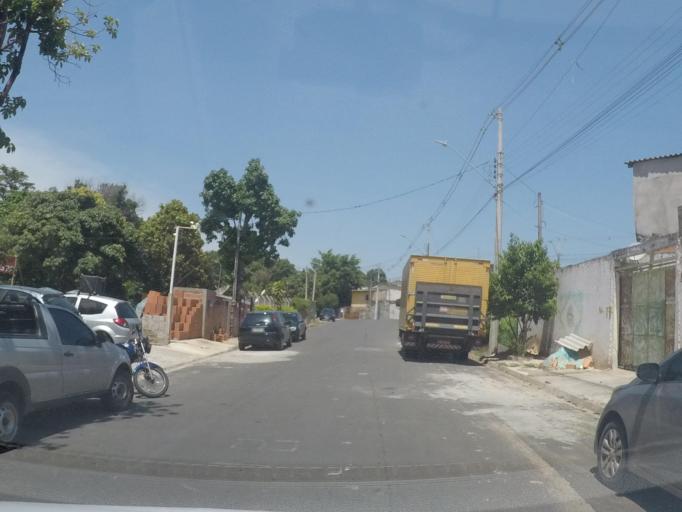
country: BR
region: Sao Paulo
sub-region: Hortolandia
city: Hortolandia
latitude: -22.8579
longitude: -47.2013
